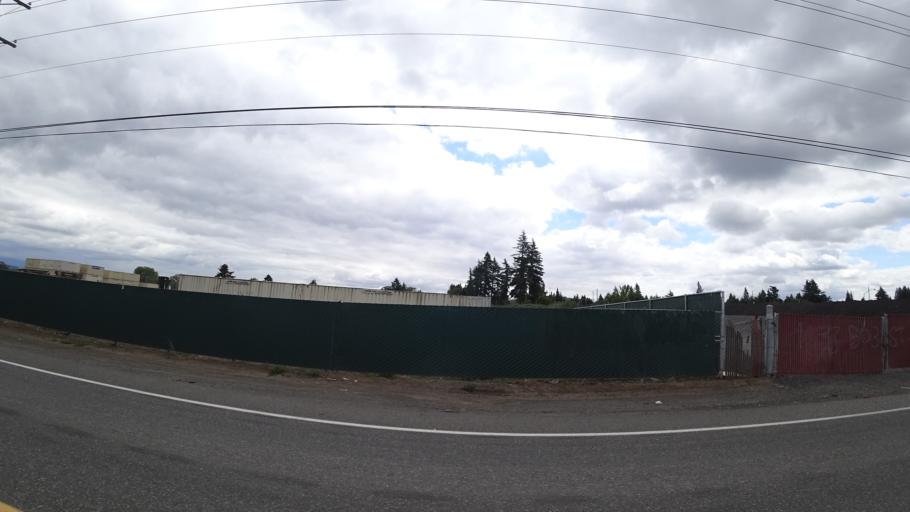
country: US
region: Oregon
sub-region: Multnomah County
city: Lents
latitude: 45.5649
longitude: -122.5923
